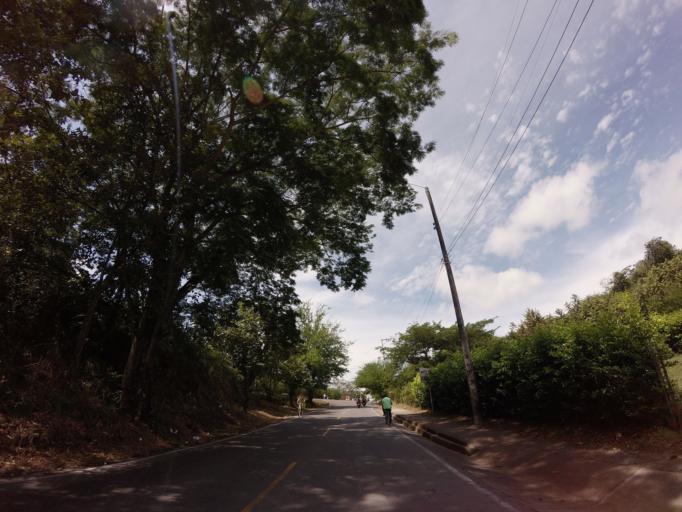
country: CO
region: Cundinamarca
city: Puerto Salgar
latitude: 5.4660
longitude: -74.6678
